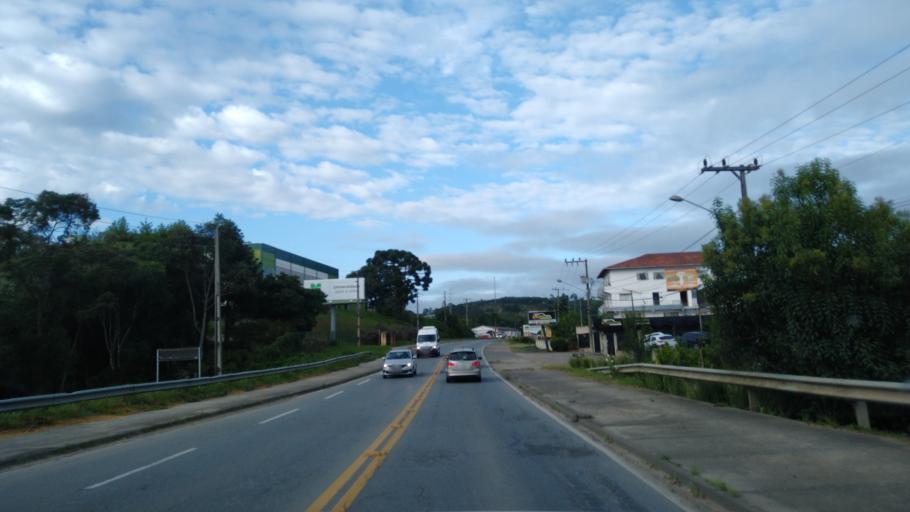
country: BR
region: Santa Catarina
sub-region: Sao Bento Do Sul
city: Sao Bento do Sul
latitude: -26.2257
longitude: -49.4168
